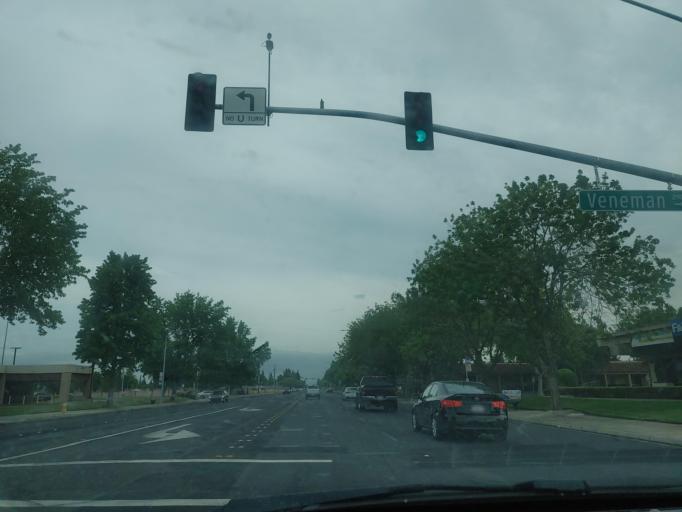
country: US
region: California
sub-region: Stanislaus County
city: Salida
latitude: 37.6893
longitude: -121.0499
